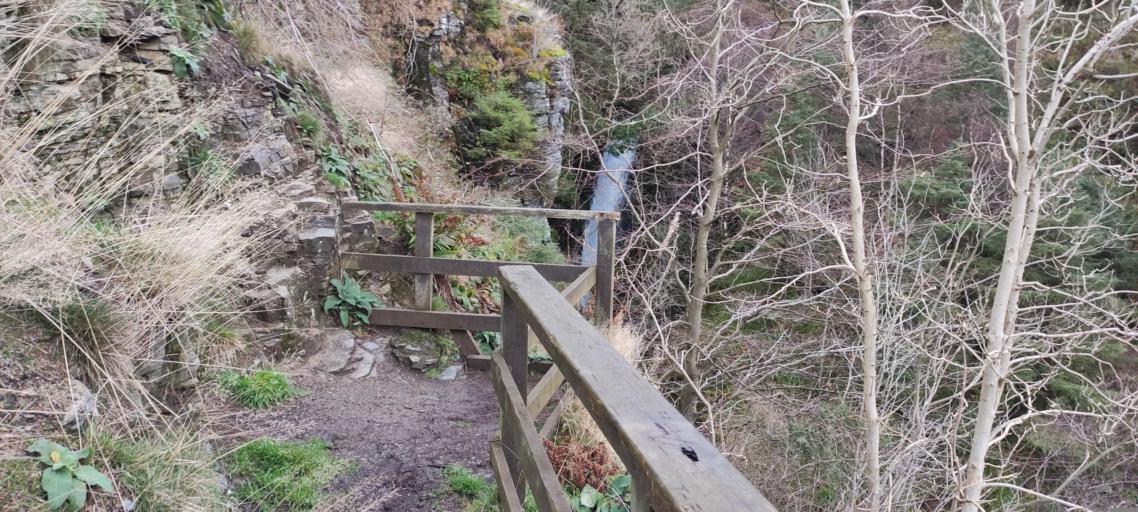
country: GB
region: England
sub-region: Cumbria
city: Cockermouth
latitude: 54.6224
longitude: -3.2695
